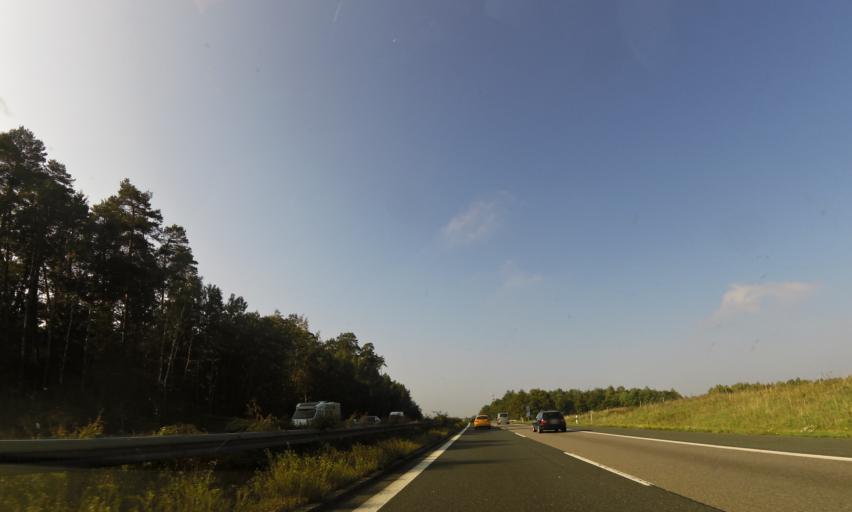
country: DE
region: Bavaria
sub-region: Regierungsbezirk Mittelfranken
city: Herrieden
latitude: 49.2629
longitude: 10.5103
